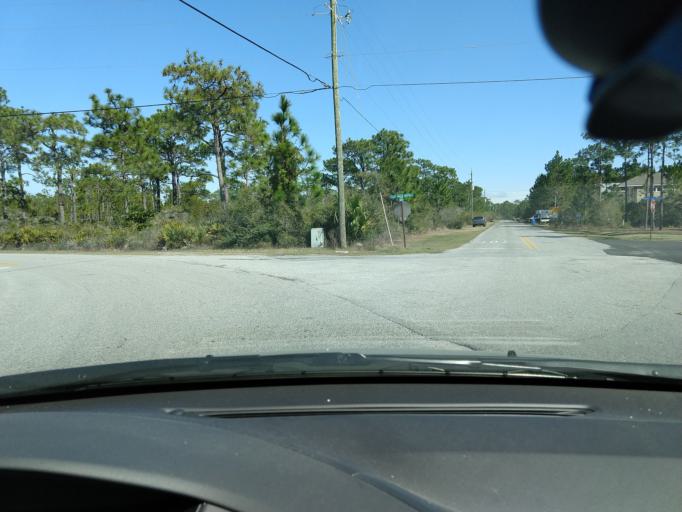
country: US
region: Florida
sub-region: Walton County
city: Miramar Beach
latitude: 30.3903
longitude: -86.3005
